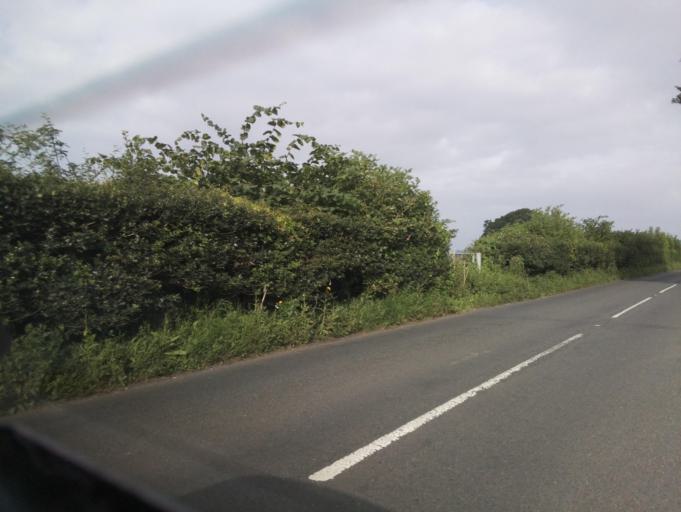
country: GB
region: England
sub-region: North Somerset
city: Long Ashton
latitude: 51.4290
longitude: -2.7036
